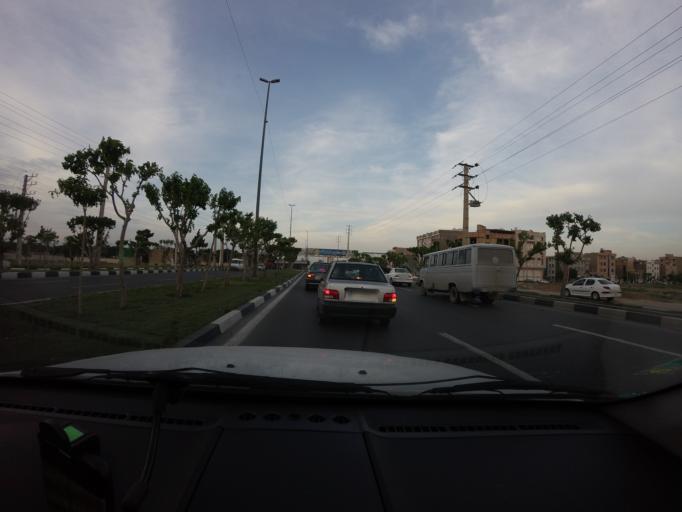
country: IR
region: Tehran
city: Eslamshahr
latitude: 35.5409
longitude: 51.2124
